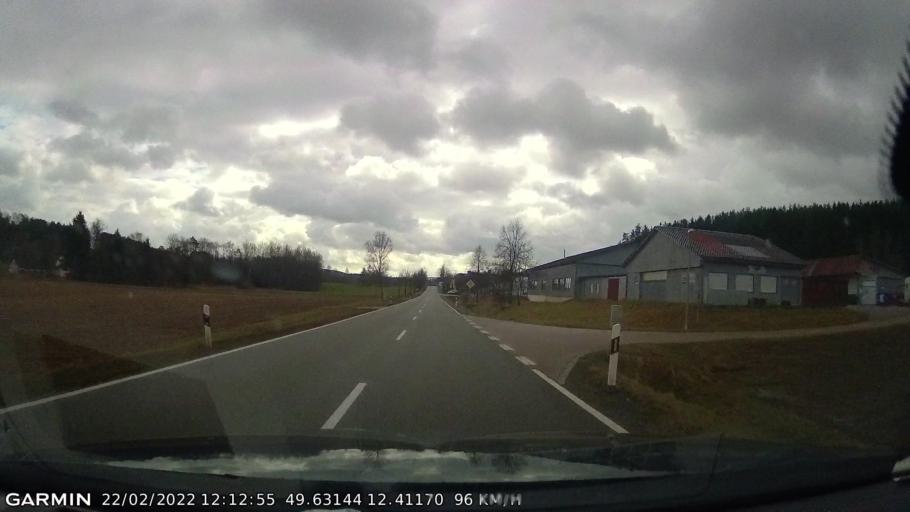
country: DE
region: Bavaria
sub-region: Upper Palatinate
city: Pleystein
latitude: 49.6311
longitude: 12.4117
